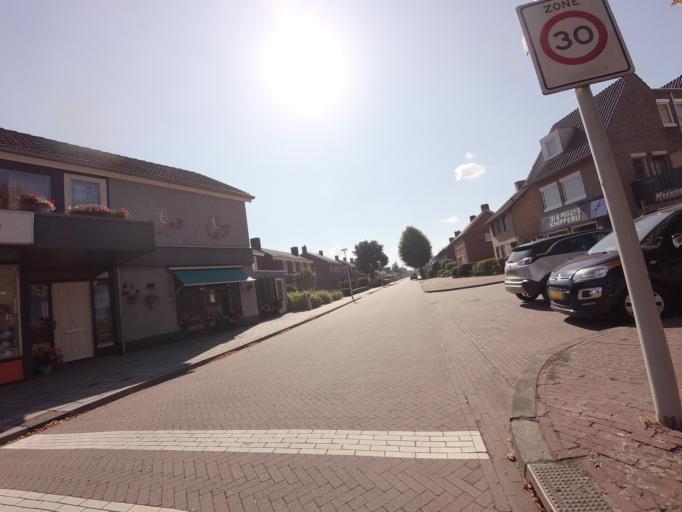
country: NL
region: North Brabant
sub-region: Gemeente Someren
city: Someren
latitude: 51.3855
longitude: 5.7152
